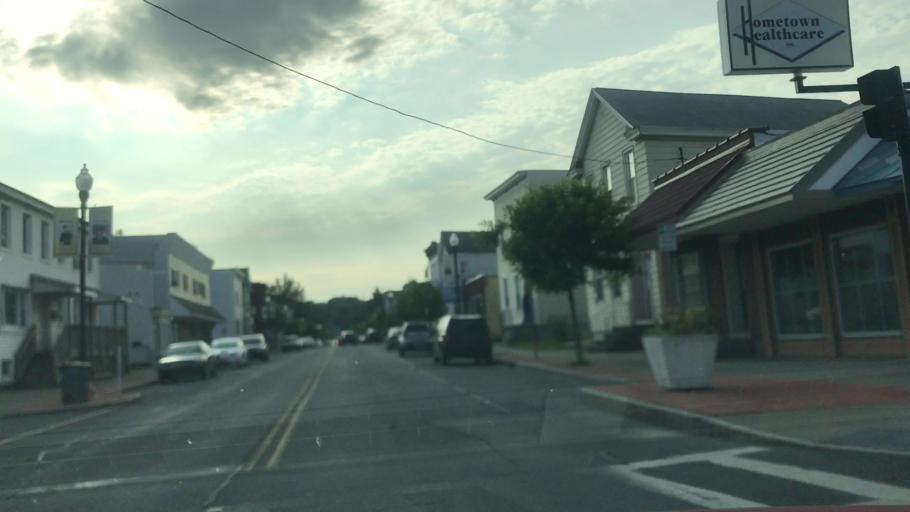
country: US
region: New York
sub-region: Albany County
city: Watervliet
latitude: 42.7312
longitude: -73.7055
